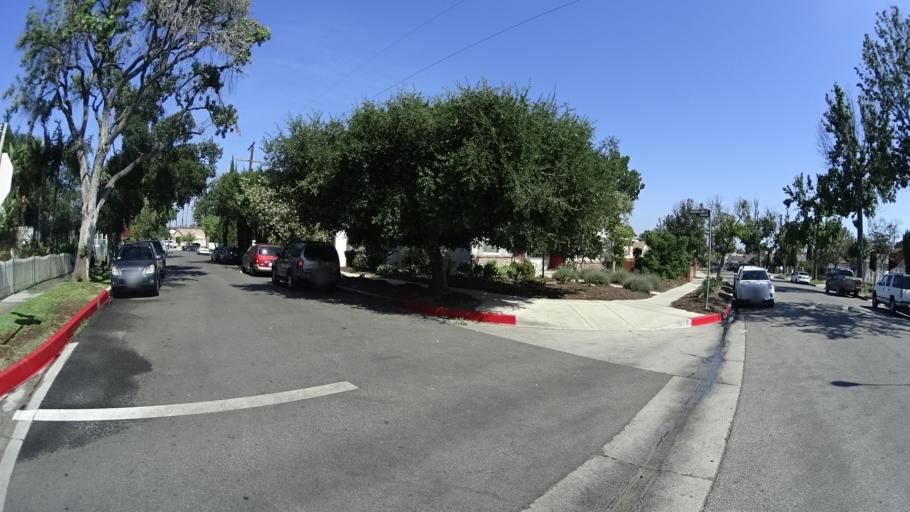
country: US
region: California
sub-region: Los Angeles County
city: Van Nuys
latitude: 34.2004
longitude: -118.4245
